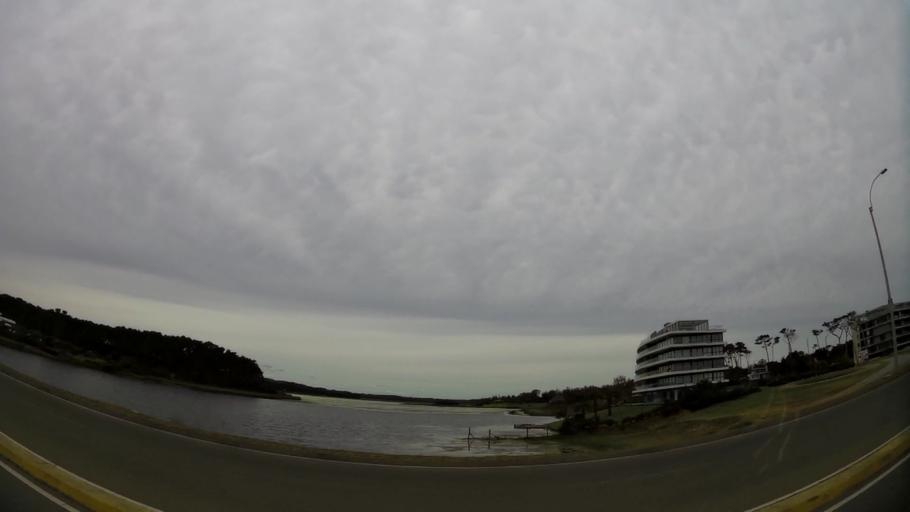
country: UY
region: Maldonado
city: Maldonado
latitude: -34.9092
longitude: -55.0065
